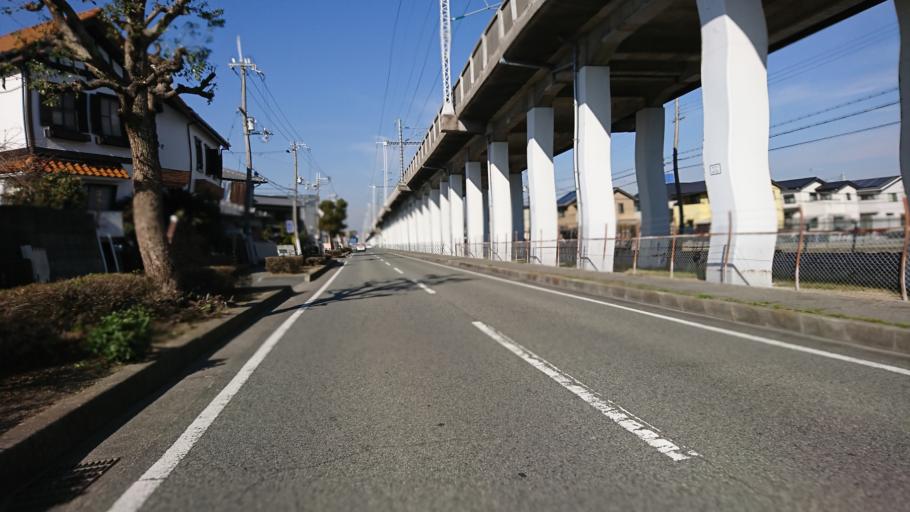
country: JP
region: Hyogo
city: Kakogawacho-honmachi
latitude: 34.7653
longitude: 134.8008
